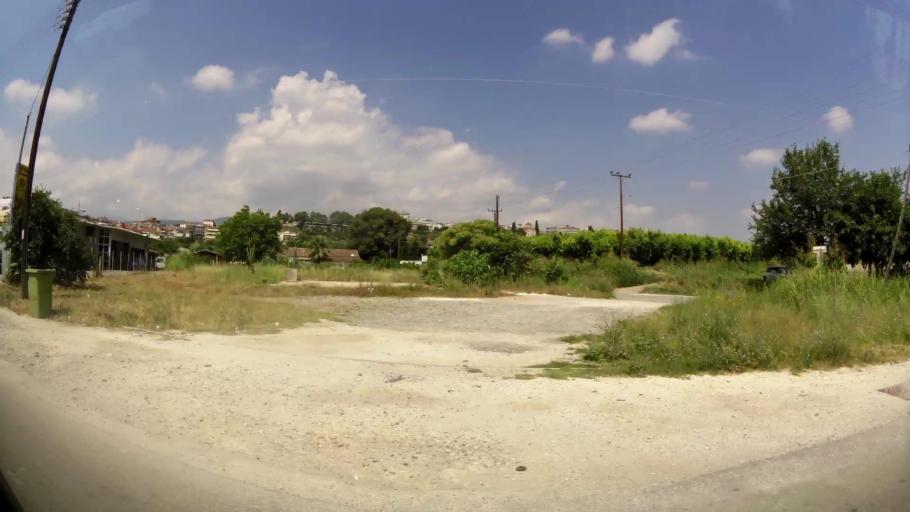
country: GR
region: Central Macedonia
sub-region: Nomos Imathias
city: Veroia
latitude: 40.5232
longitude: 22.2145
